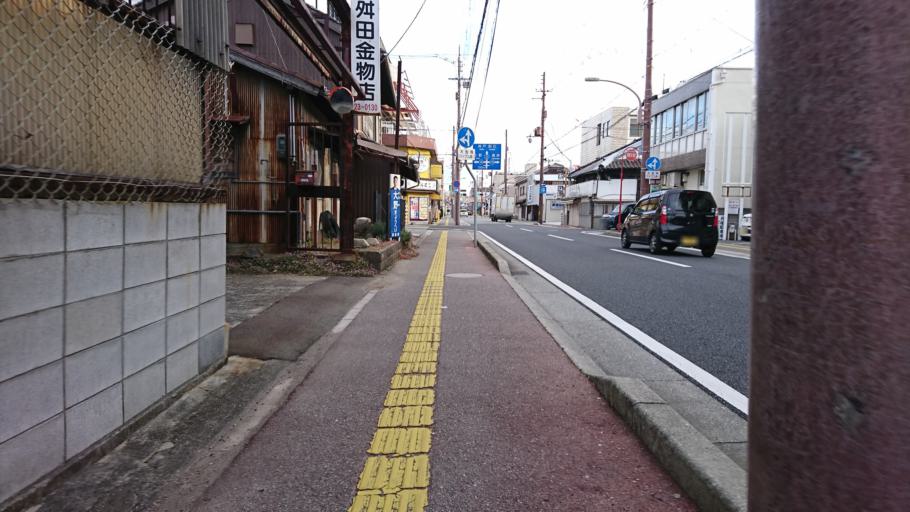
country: JP
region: Hyogo
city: Kakogawacho-honmachi
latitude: 34.7684
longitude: 134.8321
